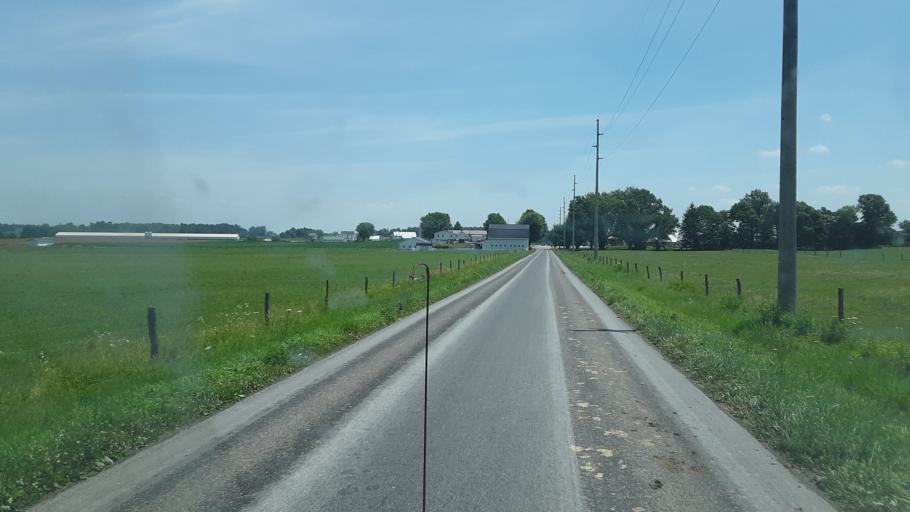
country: US
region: Ohio
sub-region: Wayne County
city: Apple Creek
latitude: 40.7118
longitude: -81.7787
